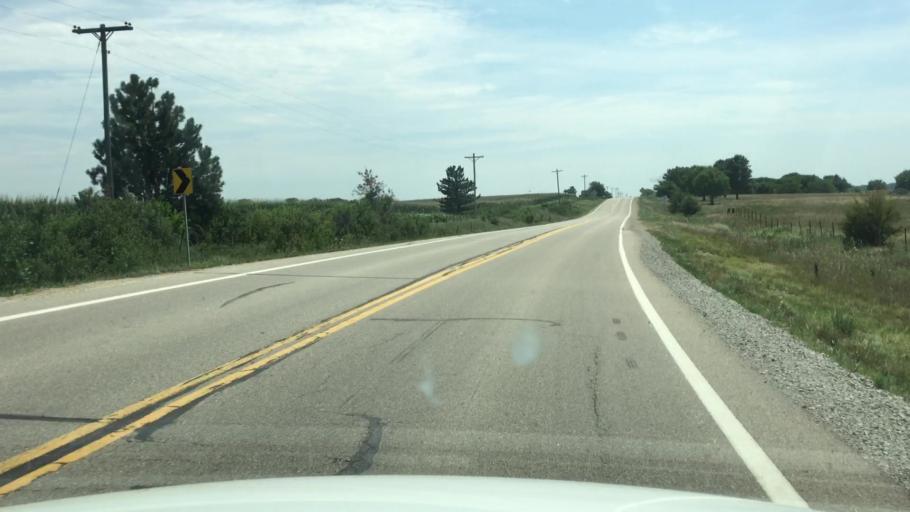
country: US
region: Kansas
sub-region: Shawnee County
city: Topeka
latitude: 38.9837
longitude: -95.4917
